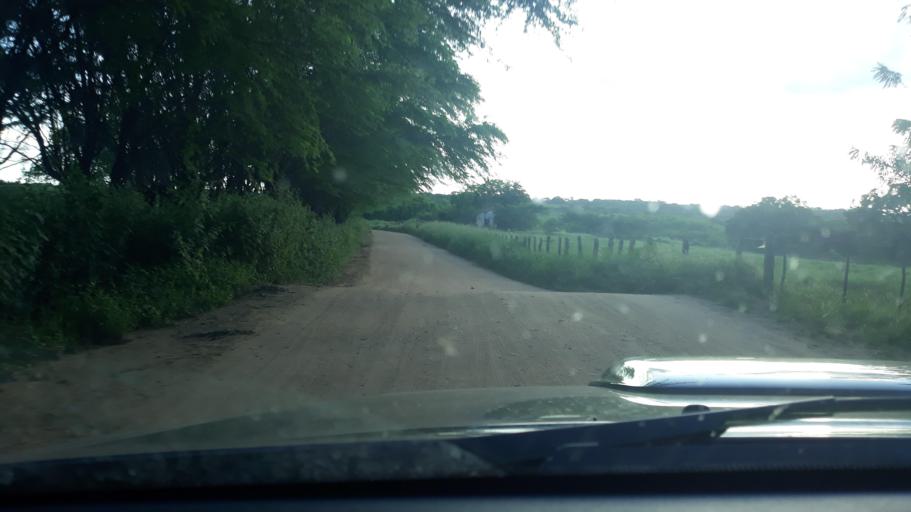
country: BR
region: Bahia
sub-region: Riacho De Santana
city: Riacho de Santana
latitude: -13.8097
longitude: -42.7185
